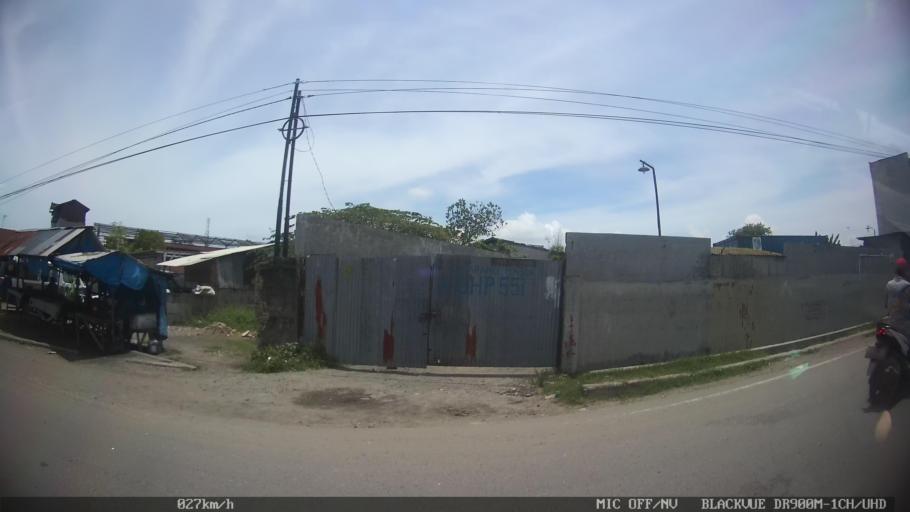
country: ID
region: North Sumatra
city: Belawan
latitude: 3.7554
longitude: 98.6763
